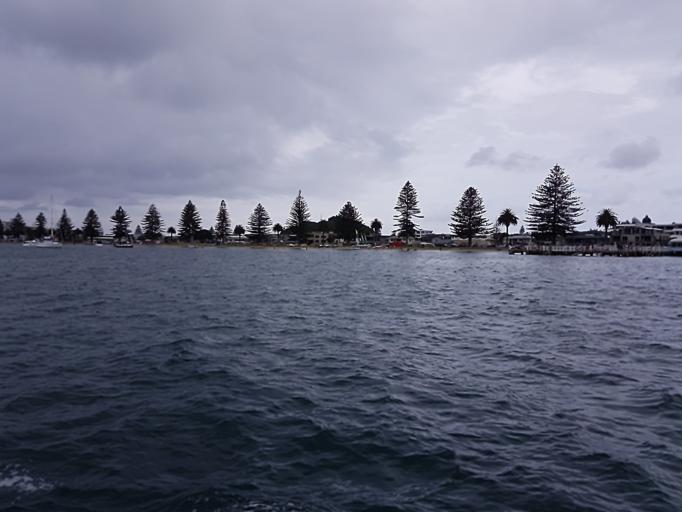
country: NZ
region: Bay of Plenty
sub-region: Tauranga City
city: Tauranga
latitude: -37.6414
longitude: 176.1801
